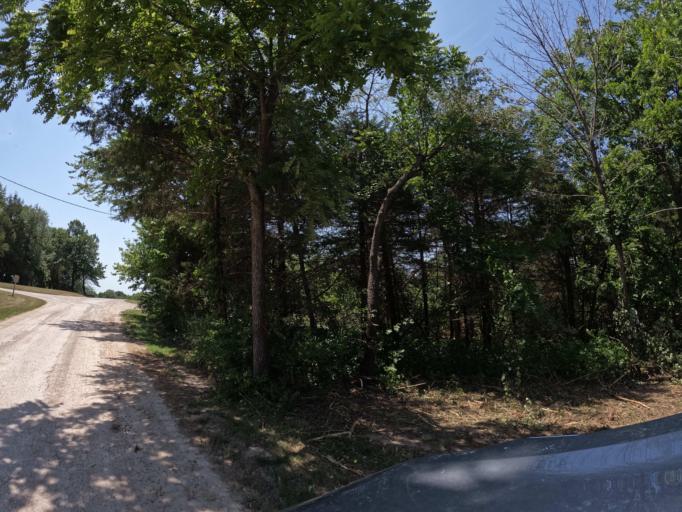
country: US
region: Iowa
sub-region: Henry County
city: Mount Pleasant
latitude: 40.9318
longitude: -91.6184
